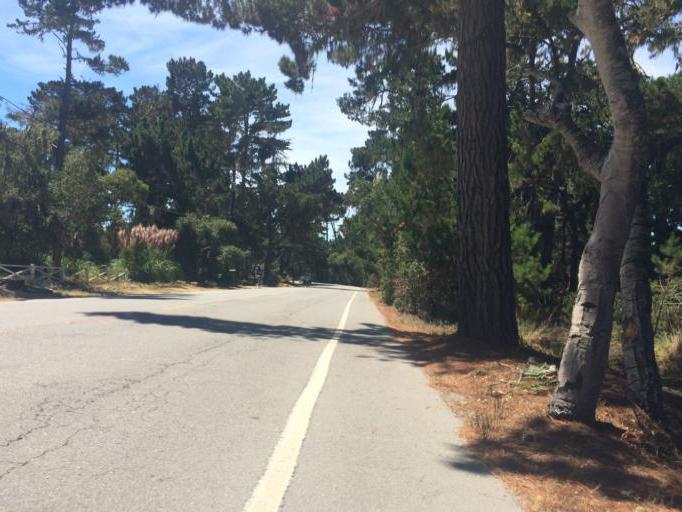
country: US
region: California
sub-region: Monterey County
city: Del Monte Forest
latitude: 36.6101
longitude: -121.9405
